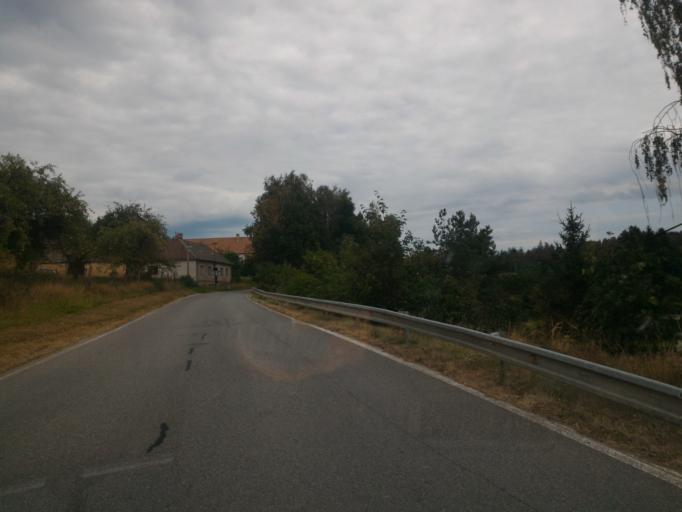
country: CZ
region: Vysocina
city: Jemnice
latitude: 49.1248
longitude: 15.5446
